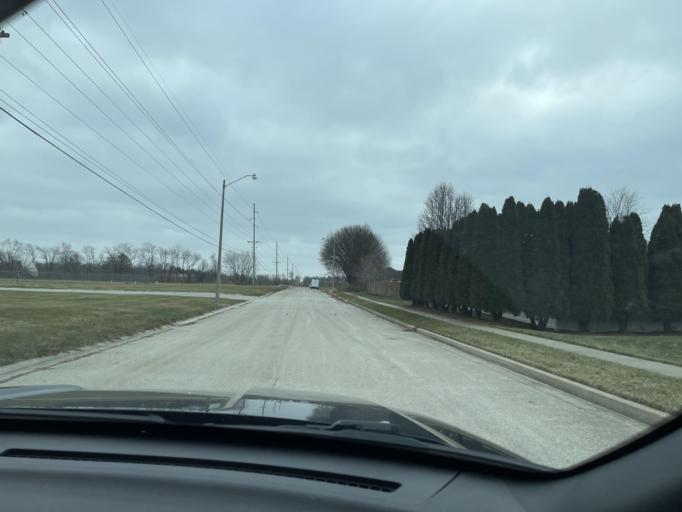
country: US
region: Illinois
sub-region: Sangamon County
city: Rochester
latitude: 39.7528
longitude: -89.5787
